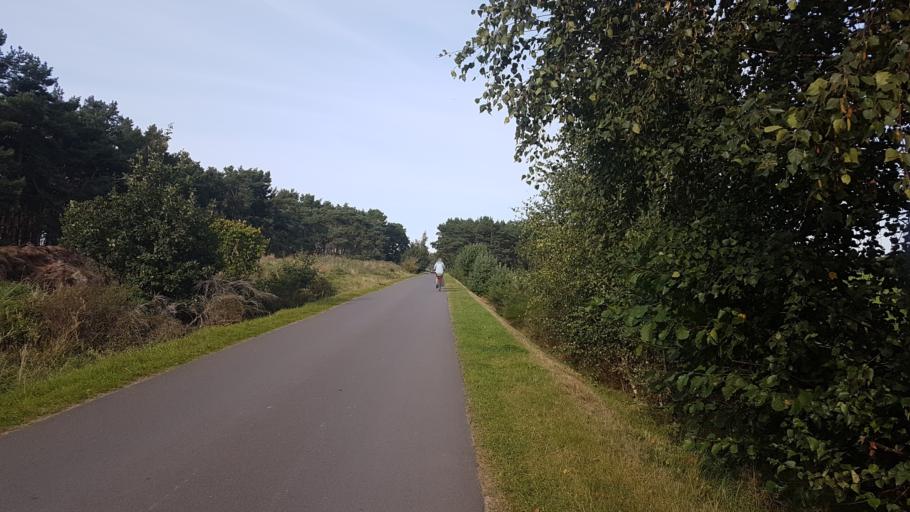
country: DE
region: Mecklenburg-Vorpommern
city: Hiddensee
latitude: 54.4679
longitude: 13.1422
